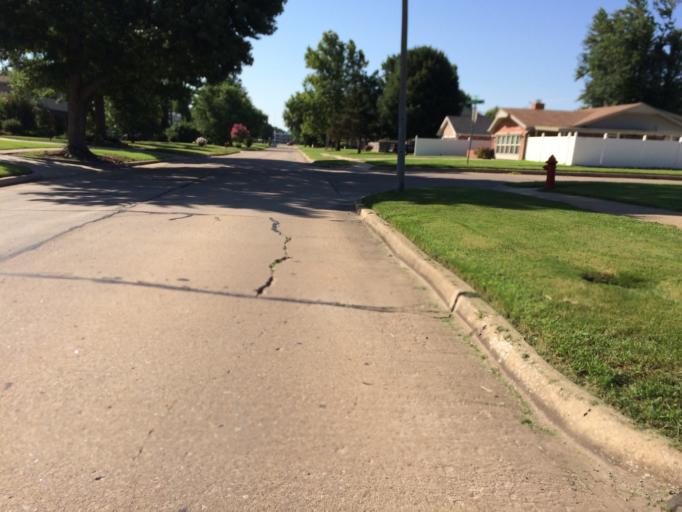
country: US
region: Oklahoma
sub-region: Cleveland County
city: Norman
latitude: 35.2304
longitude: -97.4635
